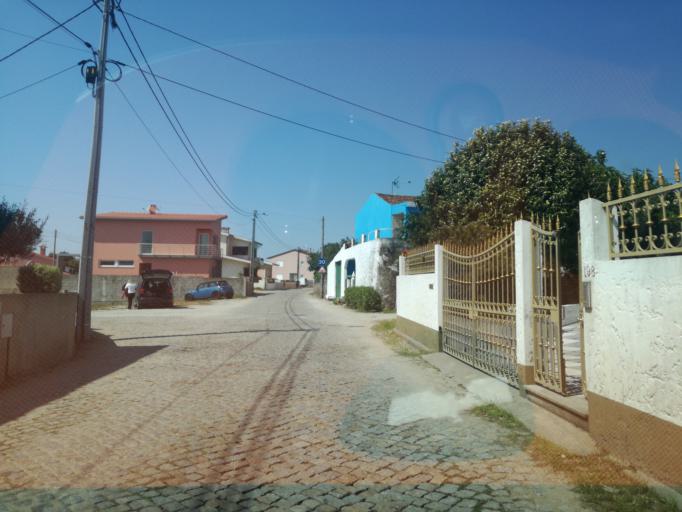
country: PT
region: Braga
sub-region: Esposende
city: Apulia
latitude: 41.4531
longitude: -8.7429
